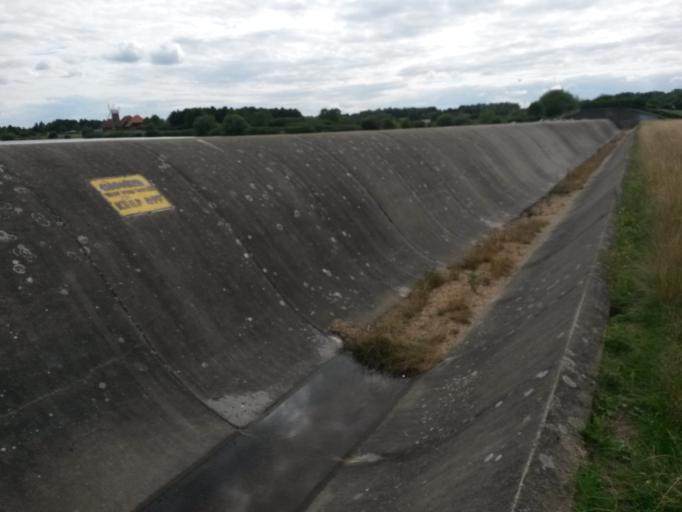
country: GB
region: England
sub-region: Milton Keynes
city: Simpson
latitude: 52.0156
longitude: -0.7058
